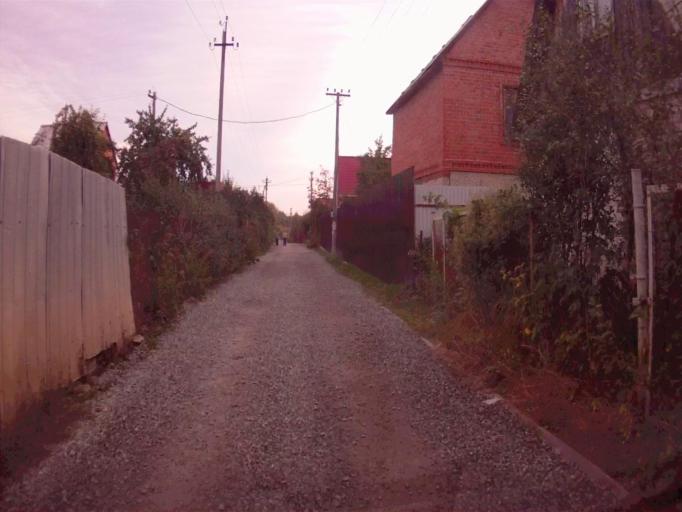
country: RU
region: Chelyabinsk
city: Sargazy
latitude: 55.1312
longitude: 61.2485
